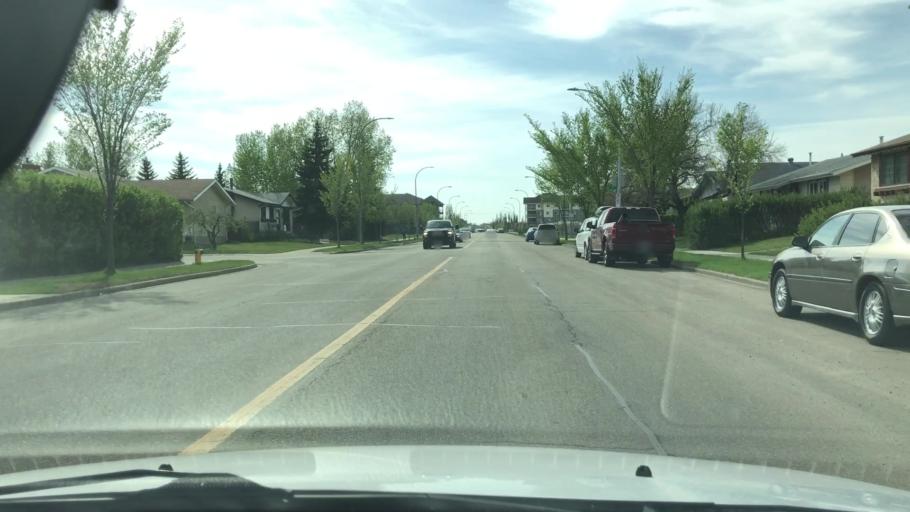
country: CA
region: Alberta
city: Edmonton
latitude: 53.6042
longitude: -113.5338
